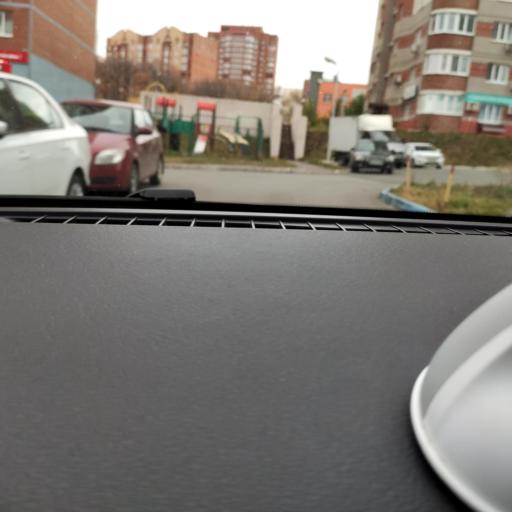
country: RU
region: Samara
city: Samara
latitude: 53.2557
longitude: 50.2008
